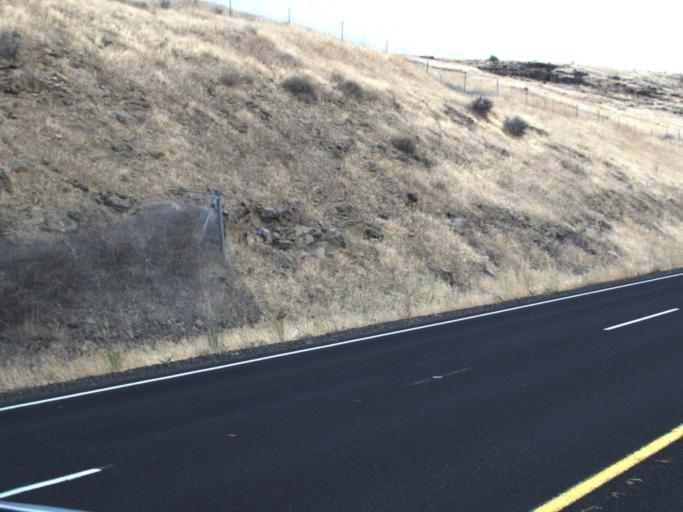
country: US
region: Washington
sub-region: Yakima County
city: Toppenish
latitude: 46.2854
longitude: -120.3638
